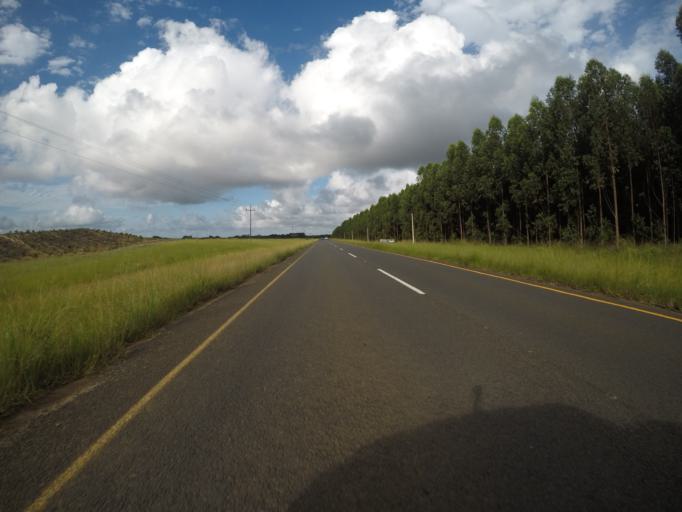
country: ZA
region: KwaZulu-Natal
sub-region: uMkhanyakude District Municipality
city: Mtubatuba
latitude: -28.3839
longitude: 32.2400
